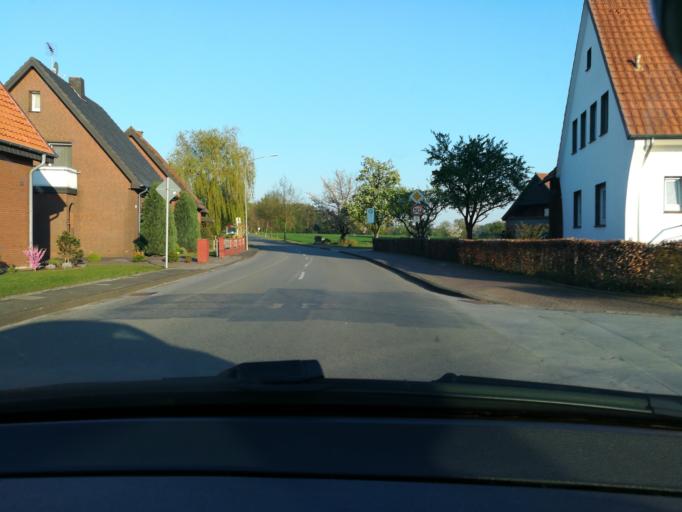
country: DE
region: Lower Saxony
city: Dissen
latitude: 52.0748
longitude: 8.2146
